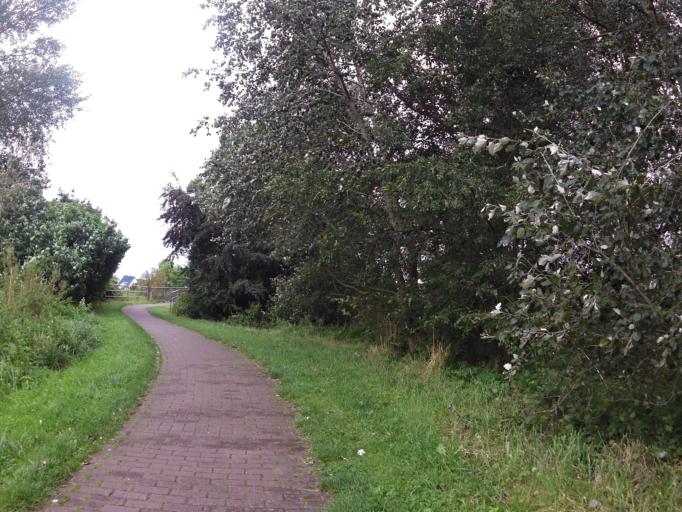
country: DE
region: Schleswig-Holstein
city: Wisch
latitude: 54.4250
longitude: 10.3684
